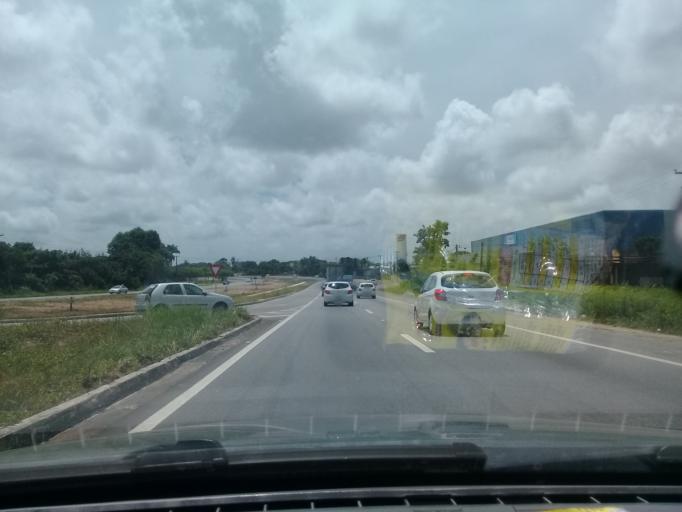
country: BR
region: Pernambuco
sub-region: Paulista
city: Paulista
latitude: -7.9632
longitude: -34.9150
